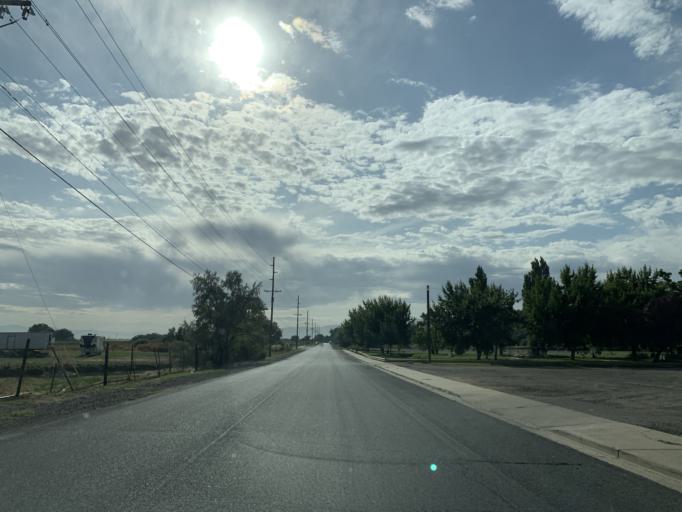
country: US
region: Utah
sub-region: Utah County
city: Provo
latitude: 40.2185
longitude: -111.6808
